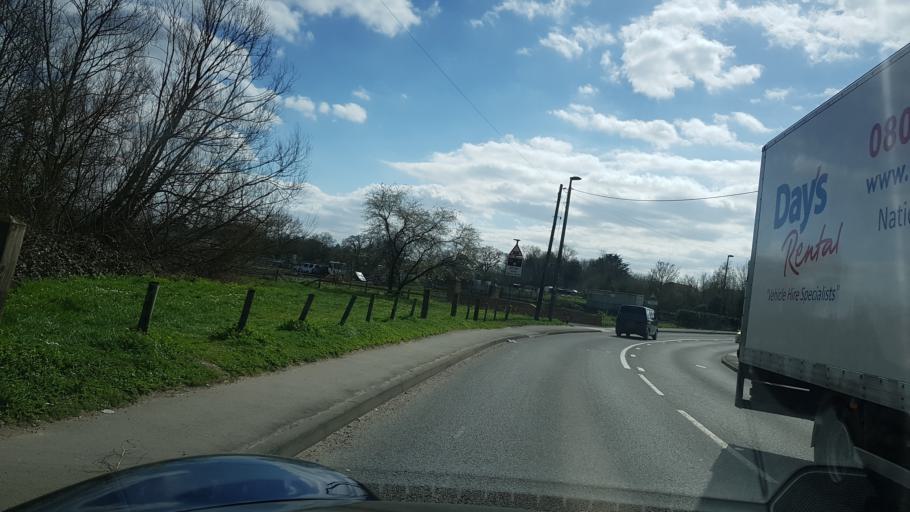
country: GB
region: England
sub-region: Surrey
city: Seale
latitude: 51.2504
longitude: -0.7116
